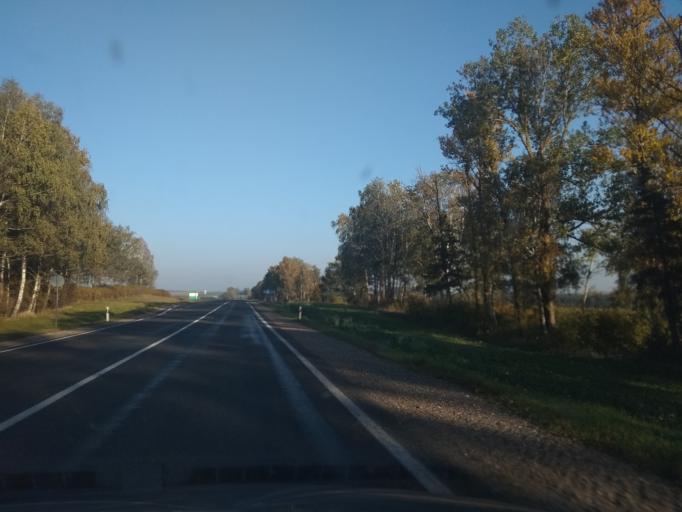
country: BY
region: Grodnenskaya
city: Vawkavysk
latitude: 53.1373
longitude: 24.2851
